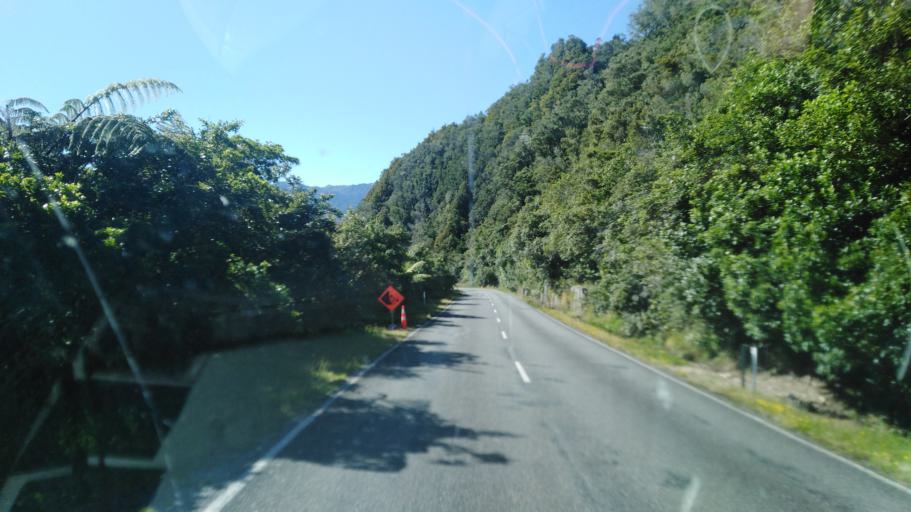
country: NZ
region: West Coast
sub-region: Buller District
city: Westport
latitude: -41.5323
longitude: 171.9542
